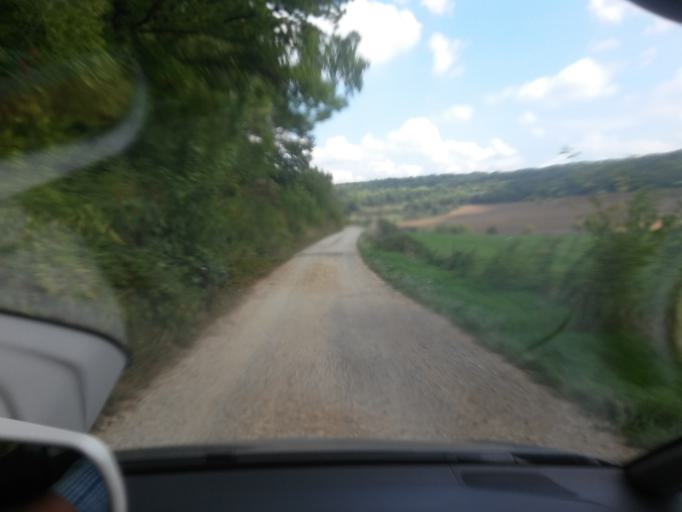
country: FR
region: Lorraine
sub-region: Departement de la Meuse
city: Montmedy
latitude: 49.5043
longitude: 5.3932
